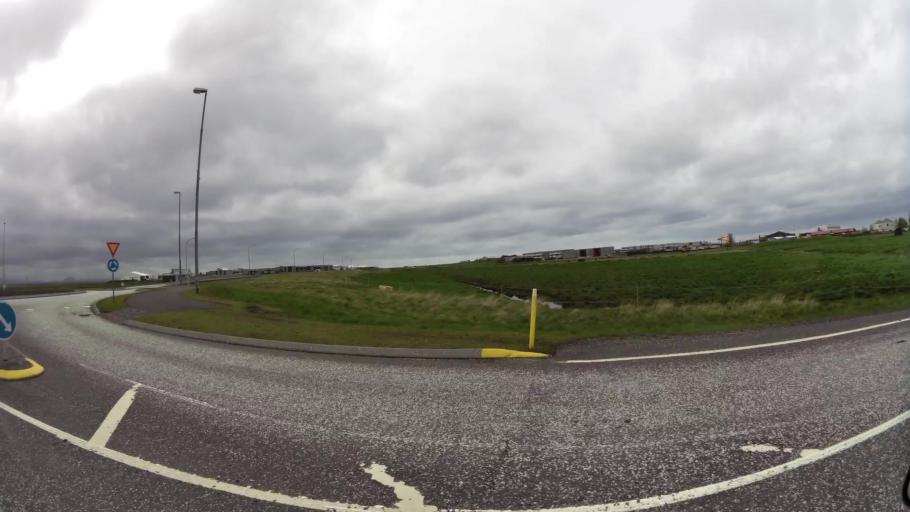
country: IS
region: Capital Region
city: Alftanes
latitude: 64.1025
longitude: -22.0097
